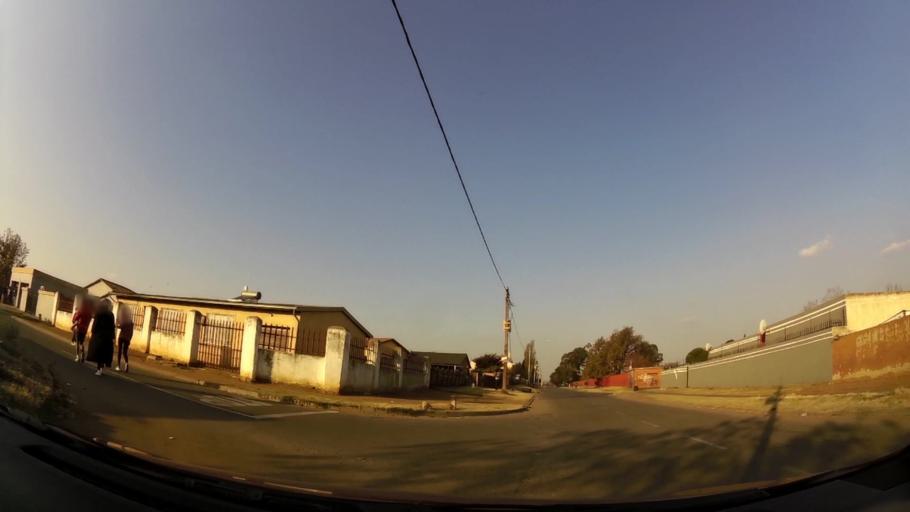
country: ZA
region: Gauteng
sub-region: City of Johannesburg Metropolitan Municipality
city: Soweto
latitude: -26.2873
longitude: 27.8952
